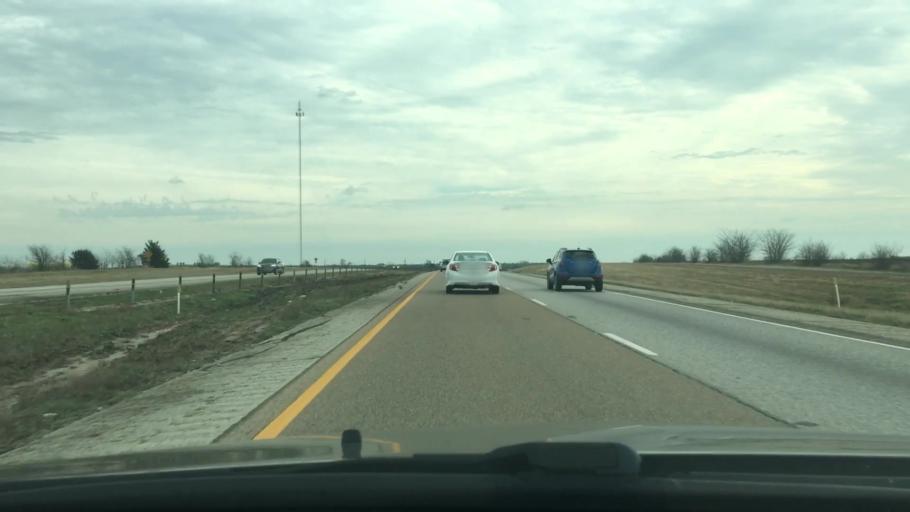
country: US
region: Texas
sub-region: Leon County
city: Centerville
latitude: 31.1079
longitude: -95.9671
